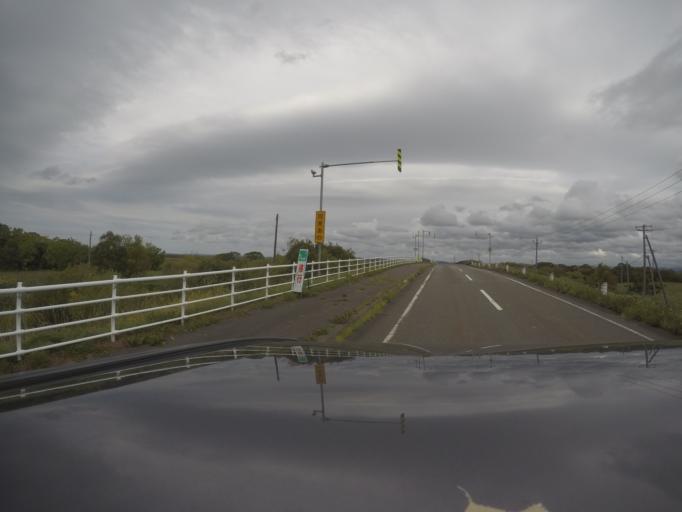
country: JP
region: Hokkaido
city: Makubetsu
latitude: 45.0036
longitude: 141.7078
